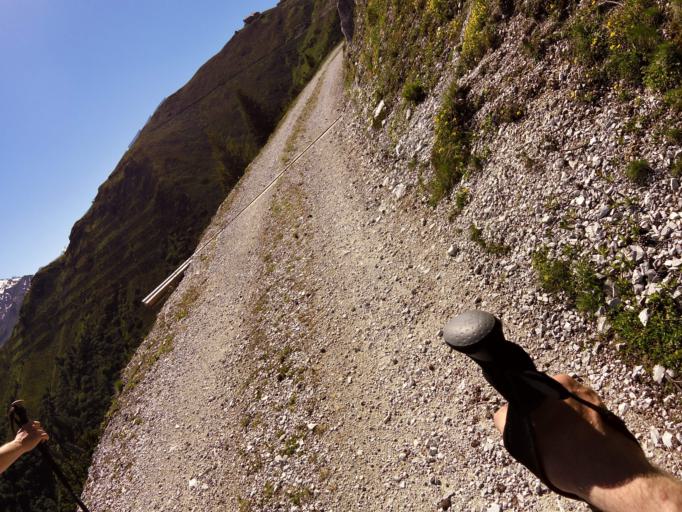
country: AT
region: Tyrol
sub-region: Politischer Bezirk Innsbruck Land
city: Neustift im Stubaital
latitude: 47.1269
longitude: 11.2902
